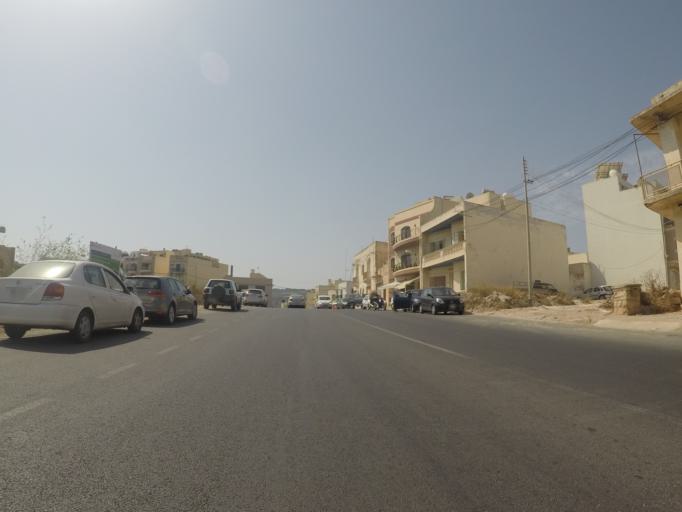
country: MT
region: L-Imgarr
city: Imgarr
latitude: 35.9219
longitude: 14.3788
